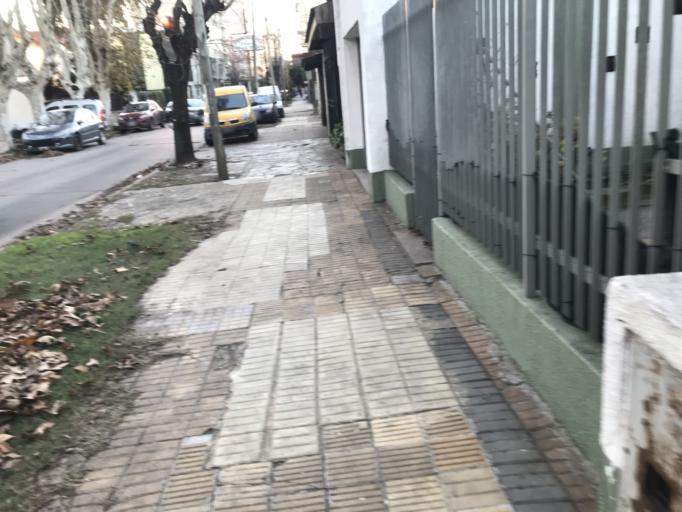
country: AR
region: Buenos Aires
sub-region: Partido de General San Martin
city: General San Martin
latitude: -34.5532
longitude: -58.5514
